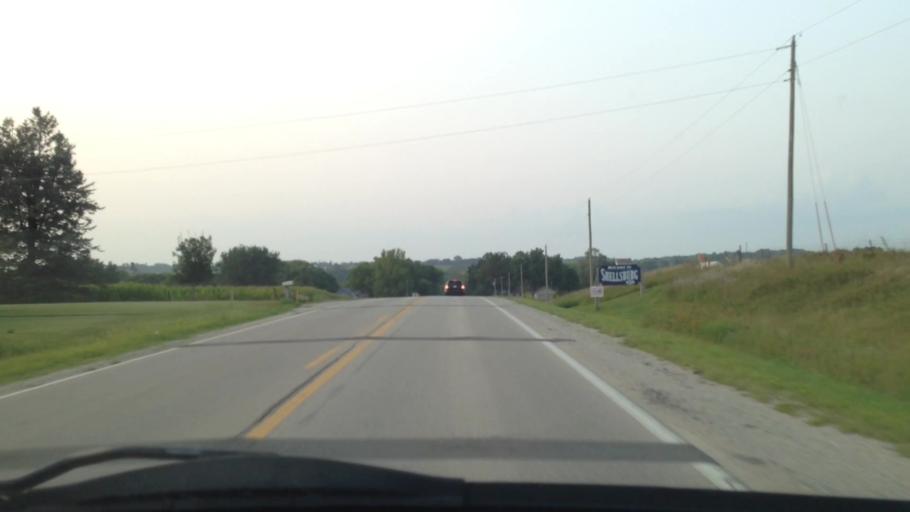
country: US
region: Iowa
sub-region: Linn County
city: Palo
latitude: 42.0849
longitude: -91.8689
